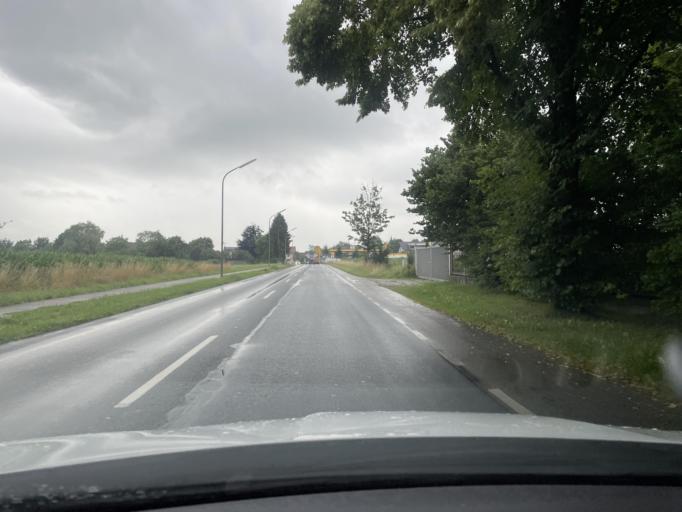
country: DE
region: Bavaria
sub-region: Upper Bavaria
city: Rosenheim
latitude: 47.8712
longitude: 12.1107
